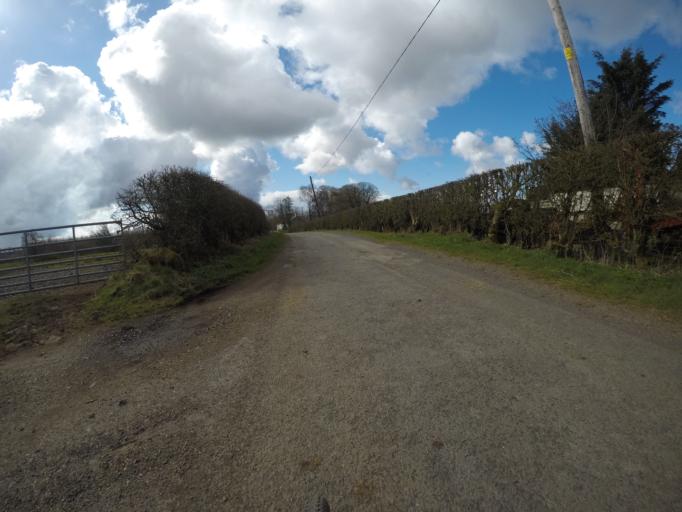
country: GB
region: Scotland
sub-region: North Ayrshire
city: Kilbirnie
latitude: 55.7223
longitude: -4.6668
